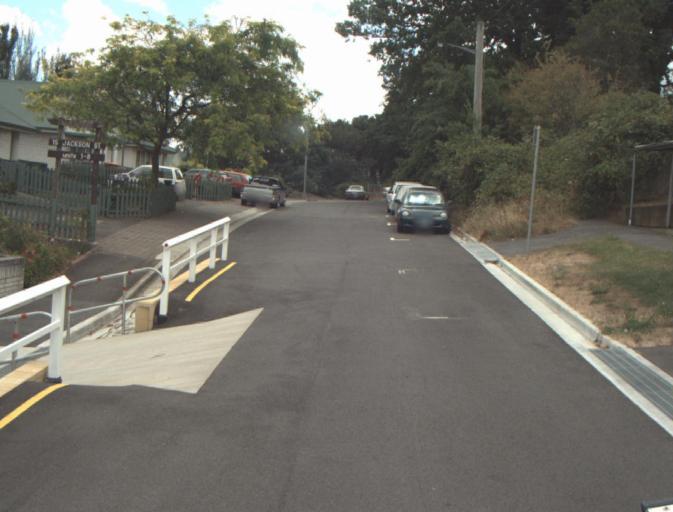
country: AU
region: Tasmania
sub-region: Launceston
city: Newnham
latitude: -41.4096
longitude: 147.1304
